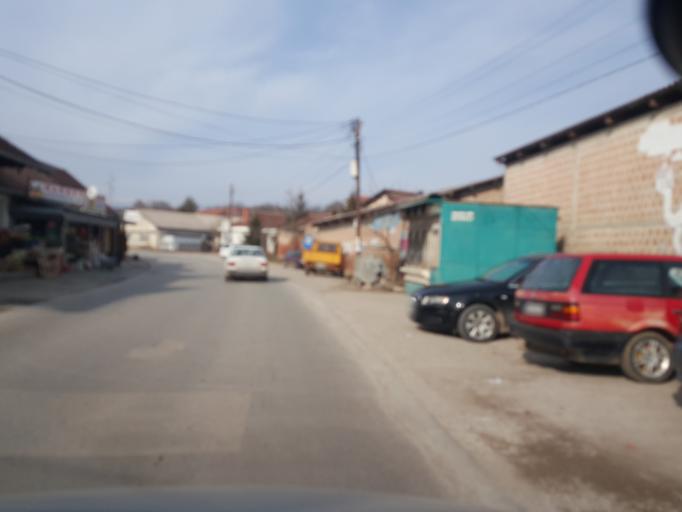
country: XK
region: Pec
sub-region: Komuna e Klines
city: Klina
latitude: 42.6625
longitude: 20.5394
